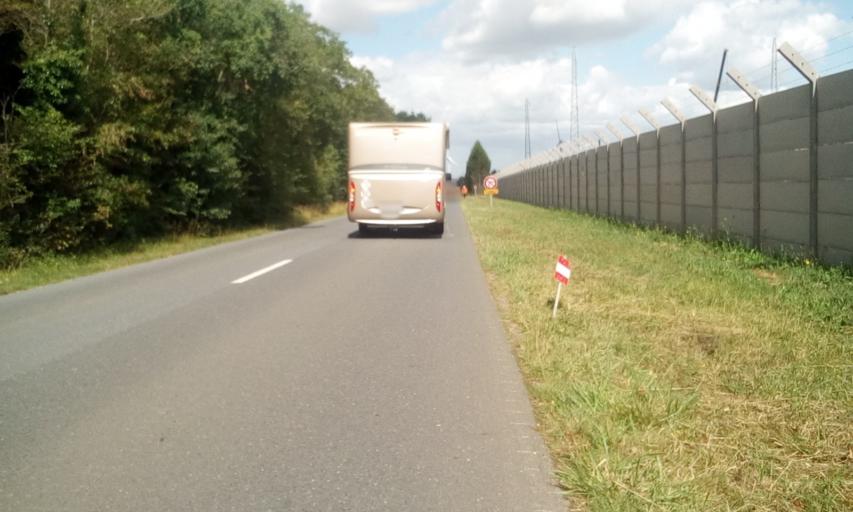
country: FR
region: Lower Normandy
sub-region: Departement du Calvados
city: Bourguebus
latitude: 49.1096
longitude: -0.2649
